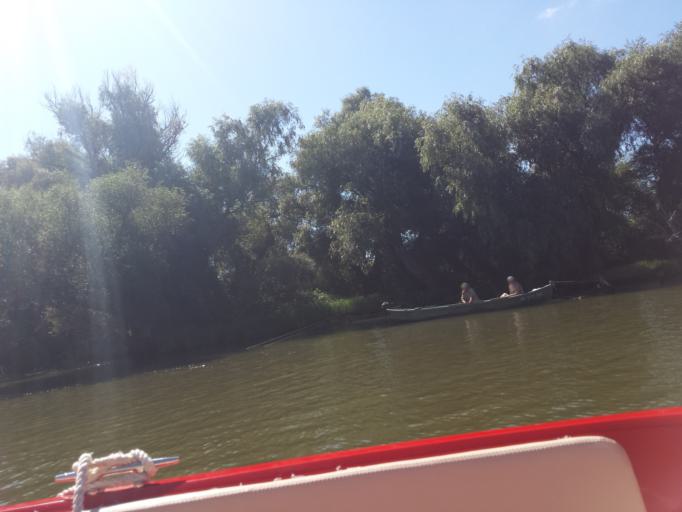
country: RO
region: Tulcea
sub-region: Comuna Mahmudia
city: Mahmudia
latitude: 45.2145
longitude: 29.1886
